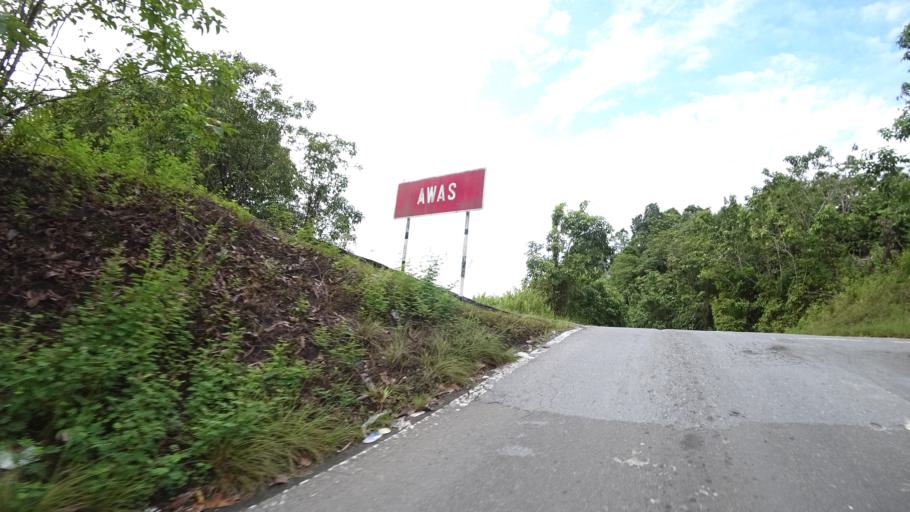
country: BN
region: Temburong
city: Bangar
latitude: 4.7920
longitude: 115.2367
